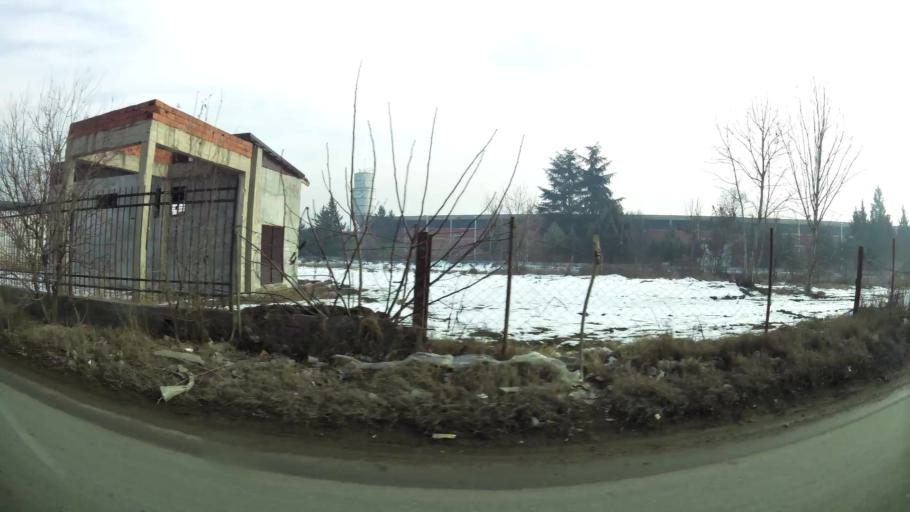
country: MK
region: Kisela Voda
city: Kisela Voda
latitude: 41.9941
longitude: 21.4924
